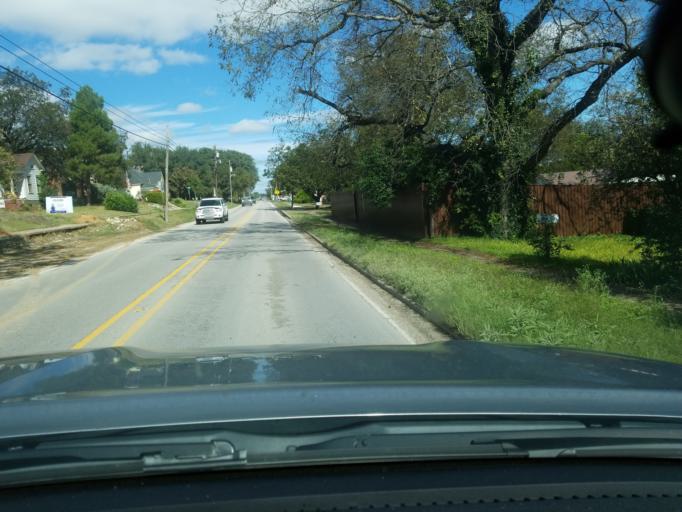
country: US
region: Texas
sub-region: Hamilton County
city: Hamilton
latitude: 31.7001
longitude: -98.1255
